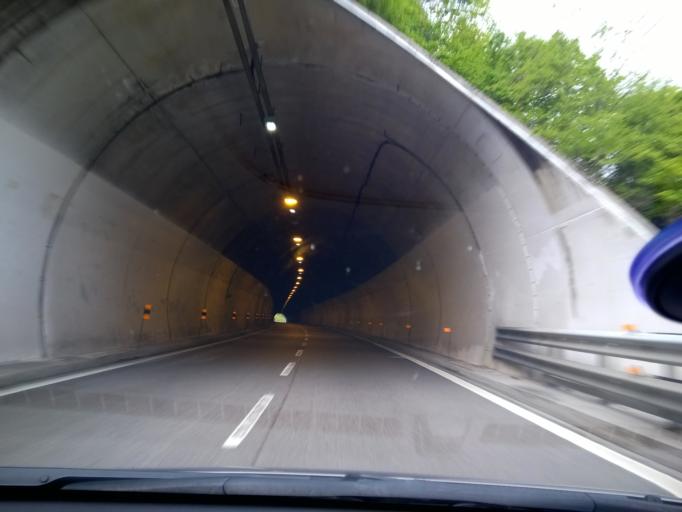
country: IT
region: Veneto
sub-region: Provincia di Belluno
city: Farra d'Alpago
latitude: 46.0879
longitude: 12.3322
